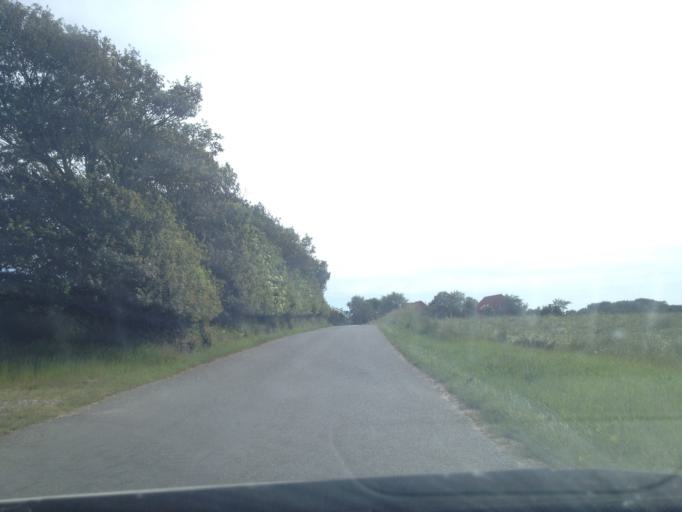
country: DK
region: Central Jutland
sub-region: Samso Kommune
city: Tranebjerg
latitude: 55.7922
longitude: 10.5565
